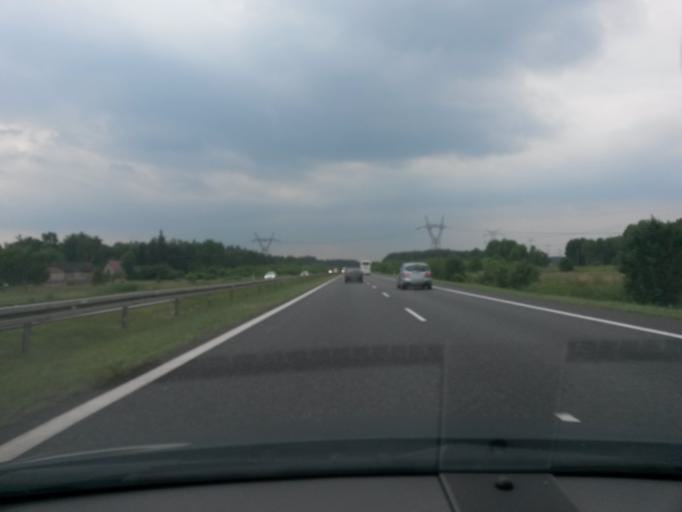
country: PL
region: Lodz Voivodeship
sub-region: Powiat radomszczanski
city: Radomsko
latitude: 51.0508
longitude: 19.3537
